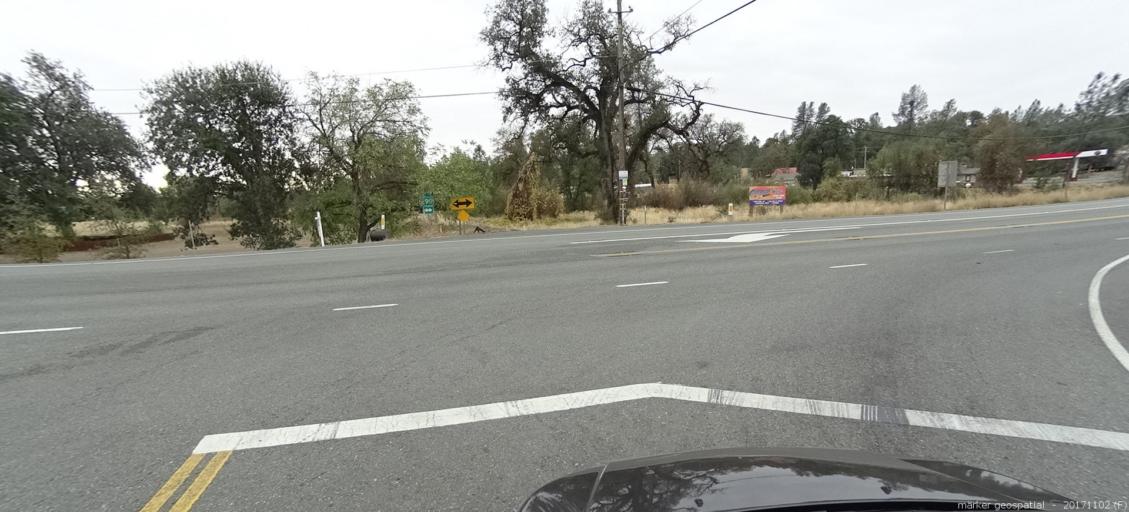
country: US
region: California
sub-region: Shasta County
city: Bella Vista
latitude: 40.6390
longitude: -122.2401
